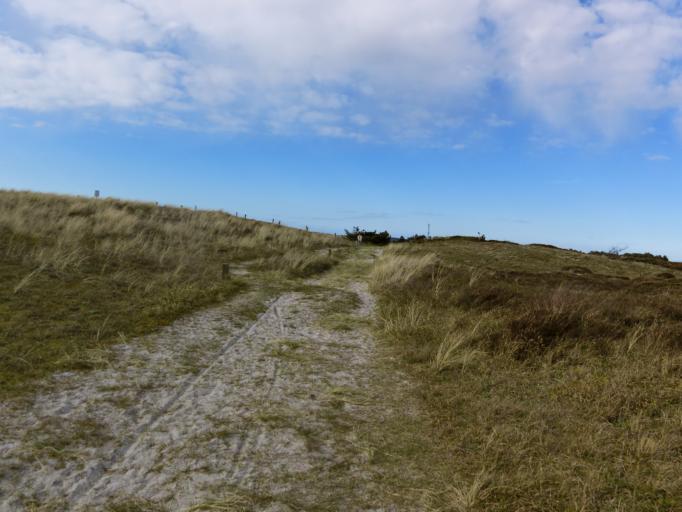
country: DE
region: Mecklenburg-Vorpommern
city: Hiddensee
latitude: 54.5508
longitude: 13.0962
